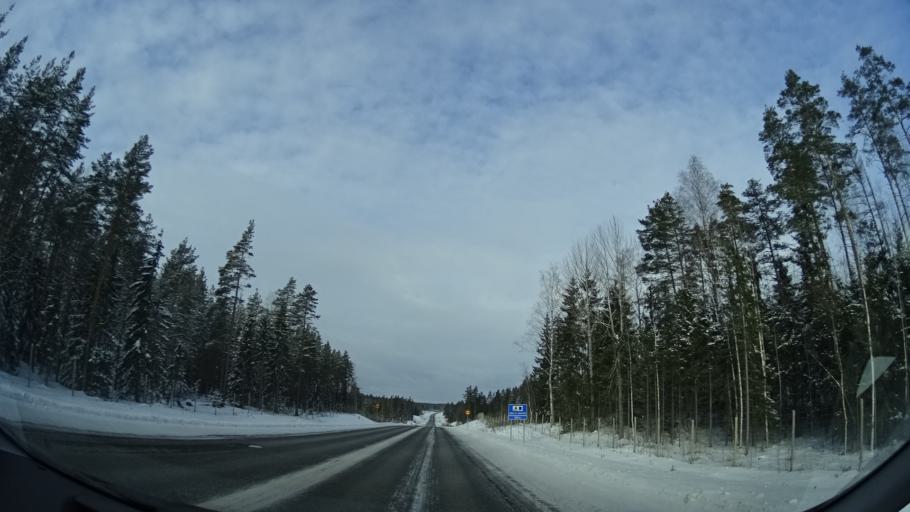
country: FI
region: Uusimaa
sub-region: Helsinki
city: Karkkila
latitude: 60.5886
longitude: 24.1173
